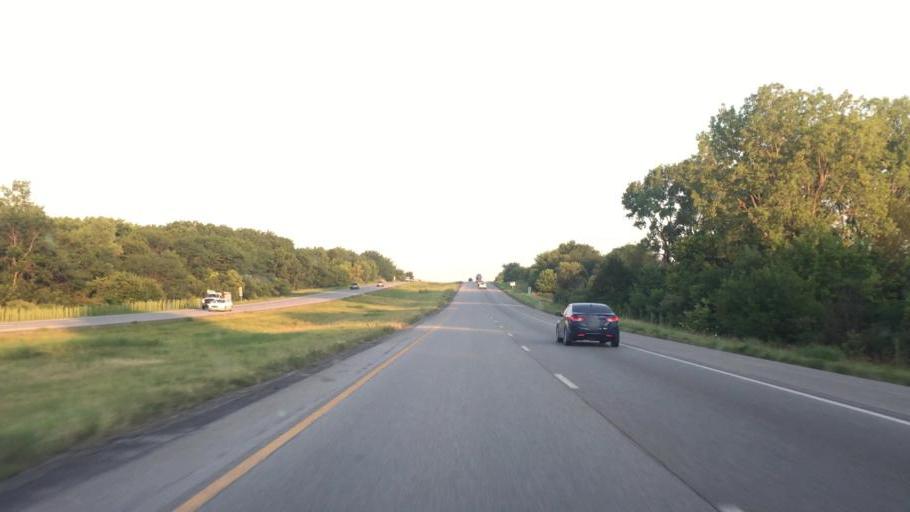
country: US
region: Missouri
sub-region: Clay County
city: Smithville
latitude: 39.3110
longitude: -94.5231
